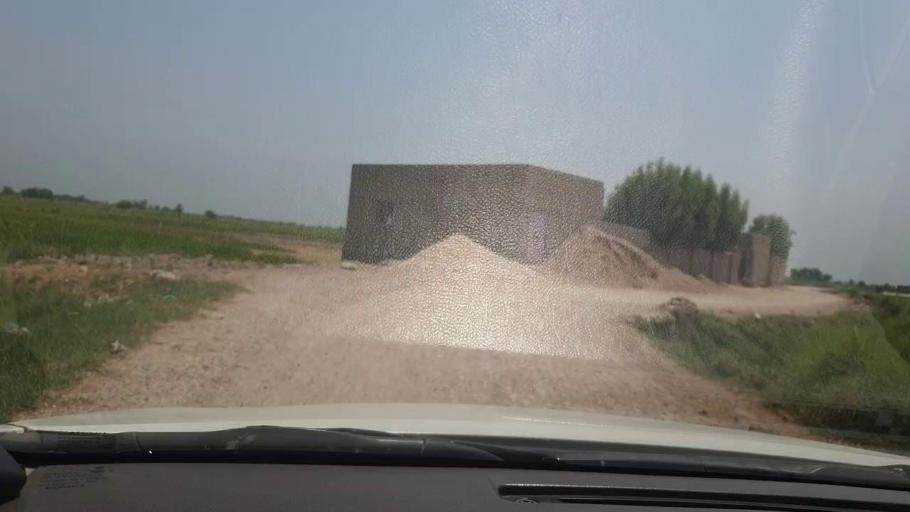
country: PK
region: Sindh
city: Garhi Yasin
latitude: 27.9273
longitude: 68.5492
